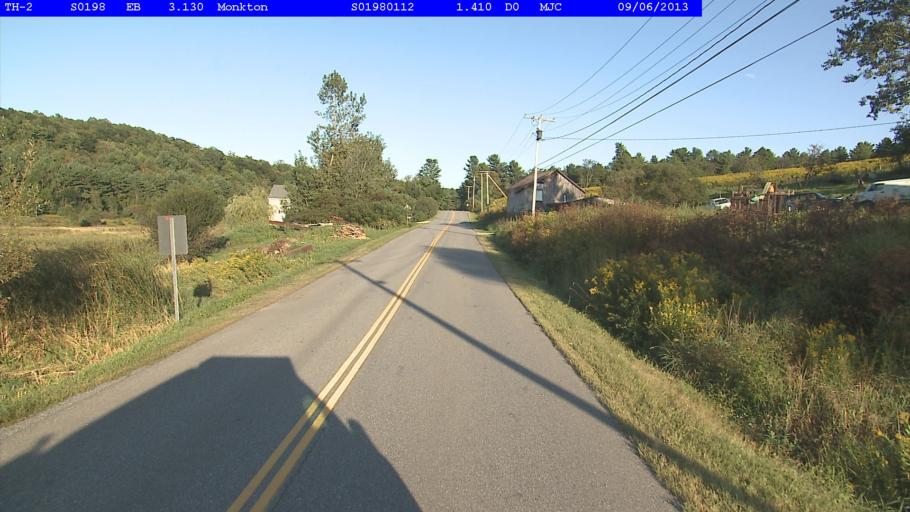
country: US
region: Vermont
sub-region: Chittenden County
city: Hinesburg
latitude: 44.2467
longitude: -73.1721
